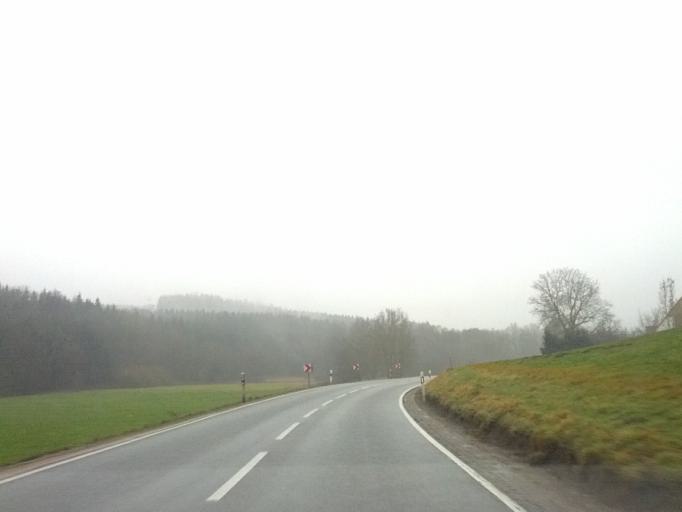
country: DE
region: Baden-Wuerttemberg
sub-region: Tuebingen Region
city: Ummendorf
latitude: 48.0768
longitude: 9.8488
